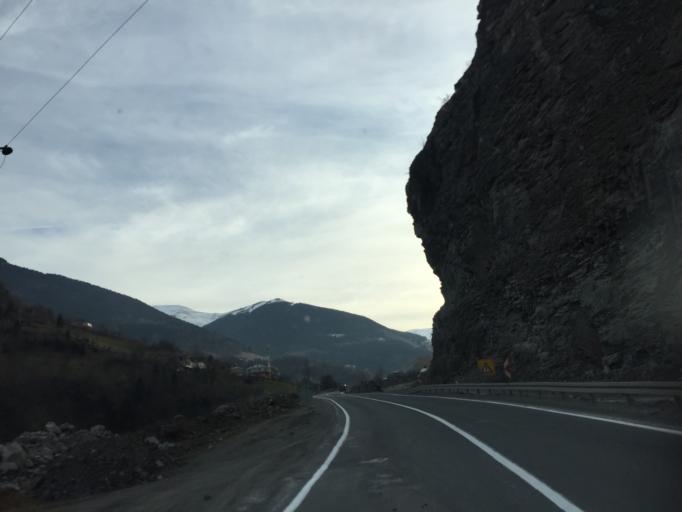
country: TR
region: Trabzon
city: Macka
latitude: 40.7261
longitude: 39.5237
